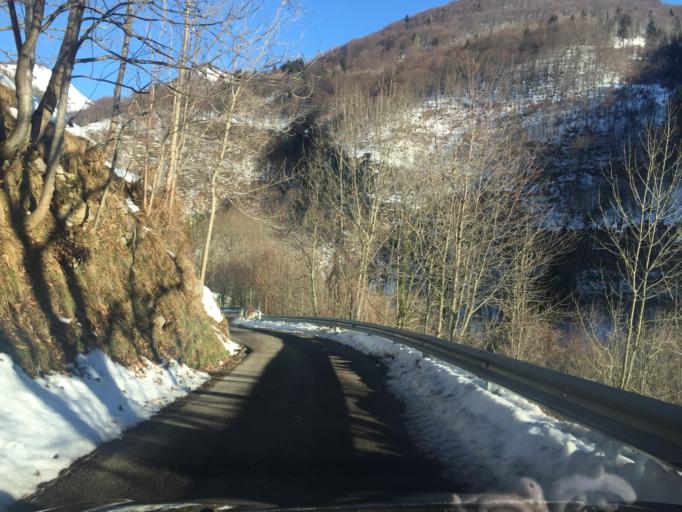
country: IT
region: Friuli Venezia Giulia
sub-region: Provincia di Udine
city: Lauco
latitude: 46.4393
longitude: 12.9706
